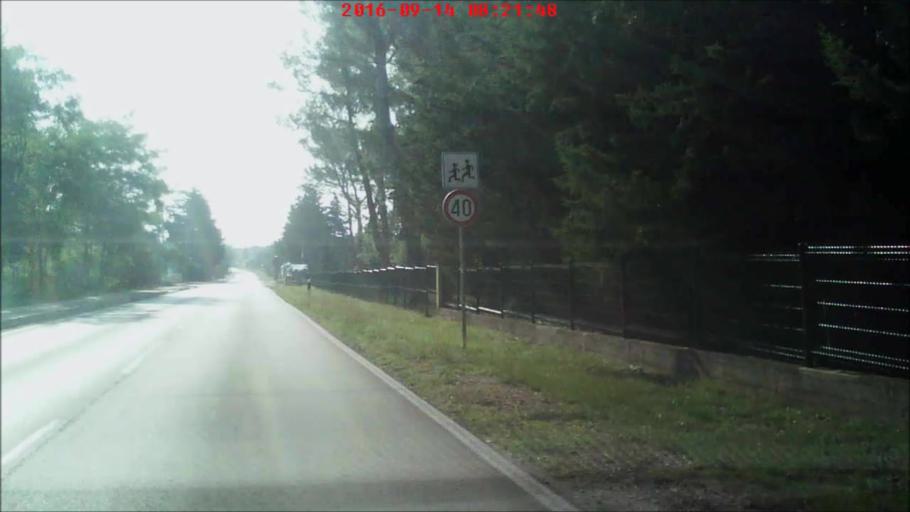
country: HR
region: Zadarska
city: Nin
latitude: 44.2202
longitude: 15.2149
